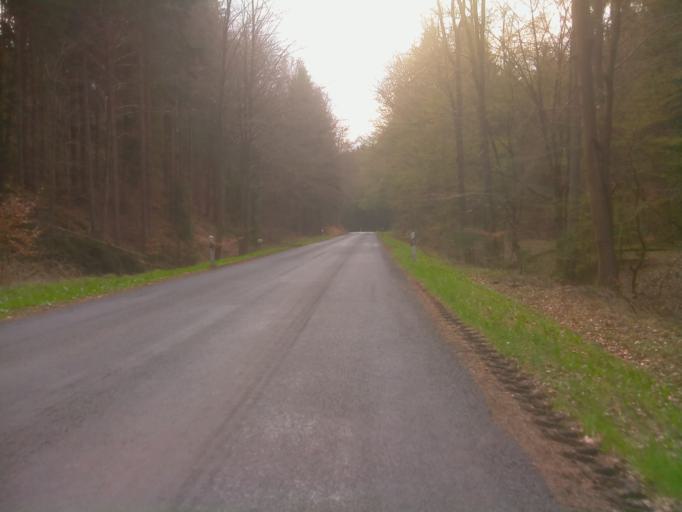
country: DE
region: Thuringia
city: Grosseutersdorf
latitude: 50.7677
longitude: 11.5721
